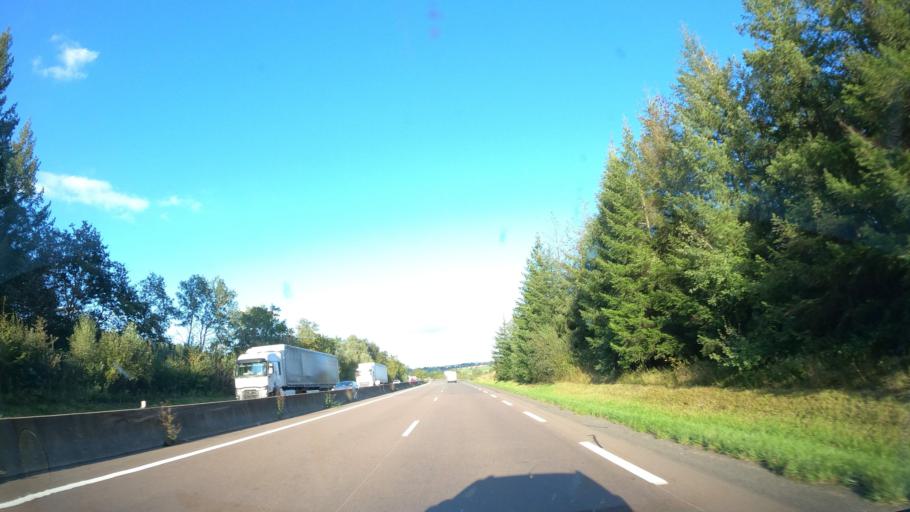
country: FR
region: Bourgogne
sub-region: Departement de Saone-et-Loire
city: Ciry-le-Noble
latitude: 46.6330
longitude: 4.3202
